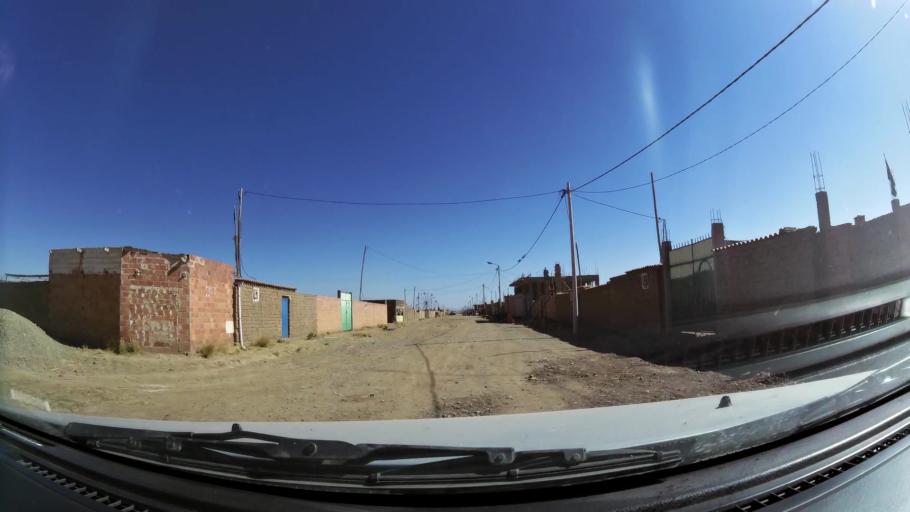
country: BO
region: La Paz
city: La Paz
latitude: -16.6138
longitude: -68.1958
